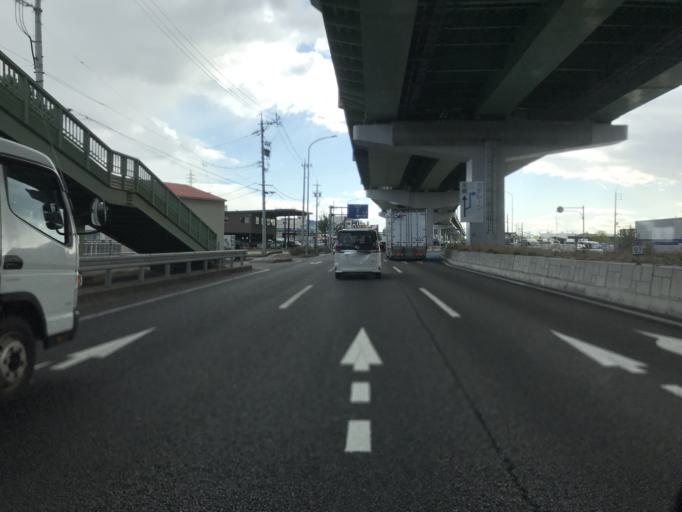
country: JP
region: Aichi
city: Komaki
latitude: 35.2657
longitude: 136.9080
